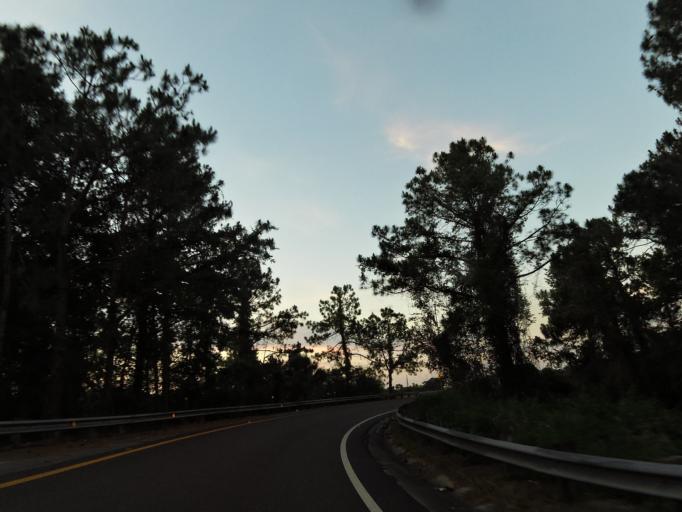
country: US
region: Florida
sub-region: Clay County
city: Orange Park
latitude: 30.1906
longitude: -81.7069
